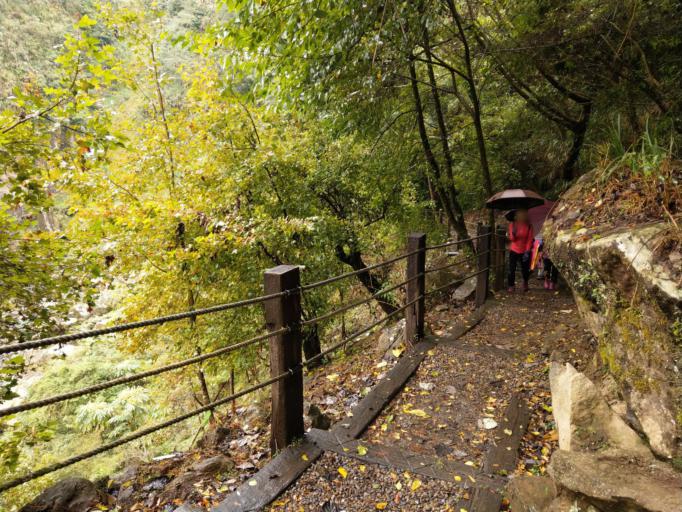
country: TW
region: Taiwan
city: Lugu
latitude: 23.6384
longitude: 120.7835
